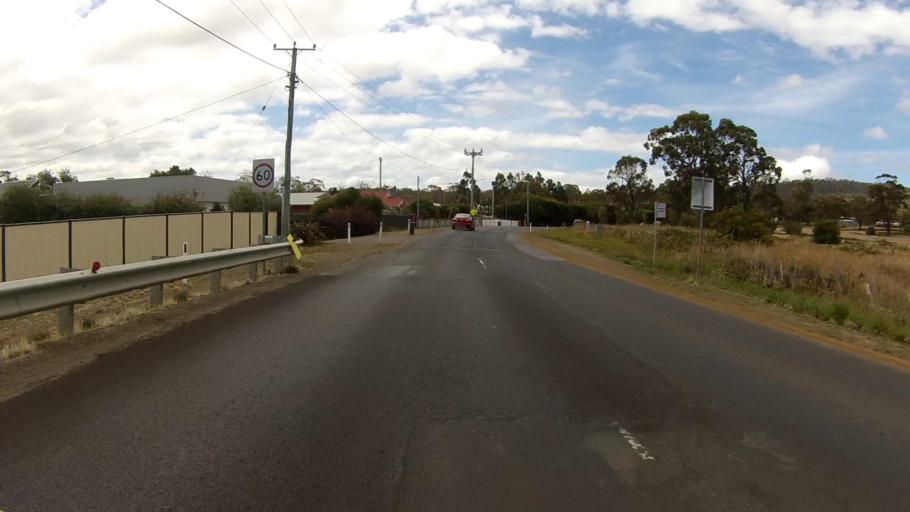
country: AU
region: Tasmania
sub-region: Sorell
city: Sorell
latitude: -42.8514
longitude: 147.6226
